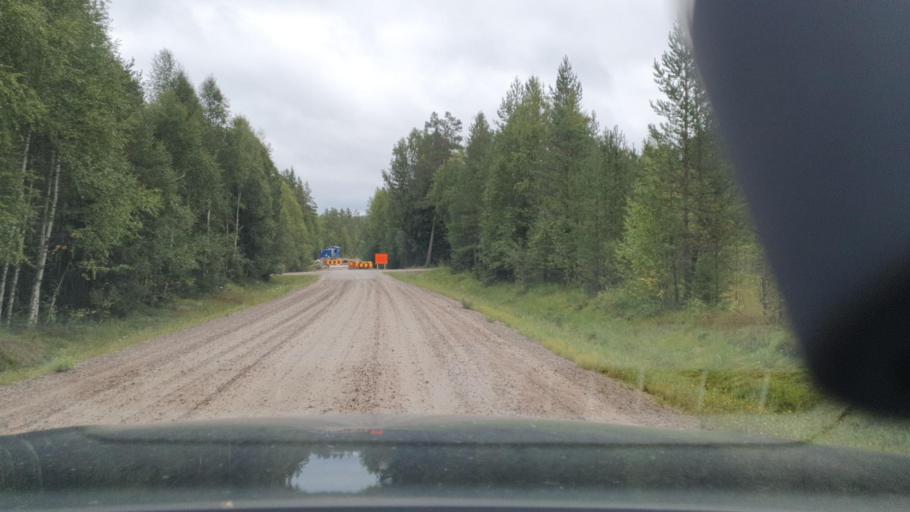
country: SE
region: Vaermland
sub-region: Torsby Kommun
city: Torsby
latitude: 60.5159
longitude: 13.0190
